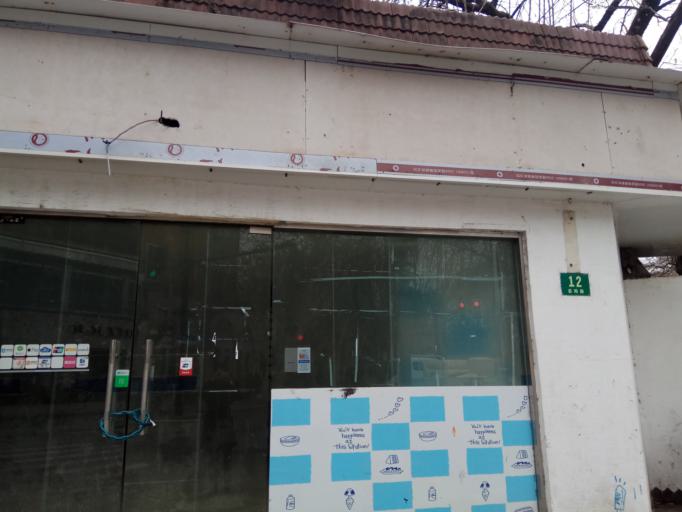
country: CN
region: Shanghai Shi
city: Xuhui
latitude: 31.2105
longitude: 121.4471
